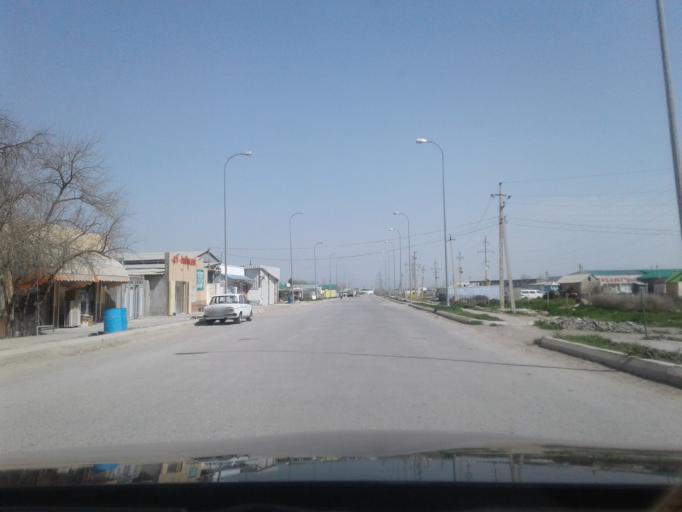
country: TM
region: Ahal
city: Abadan
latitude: 38.1580
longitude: 57.9748
